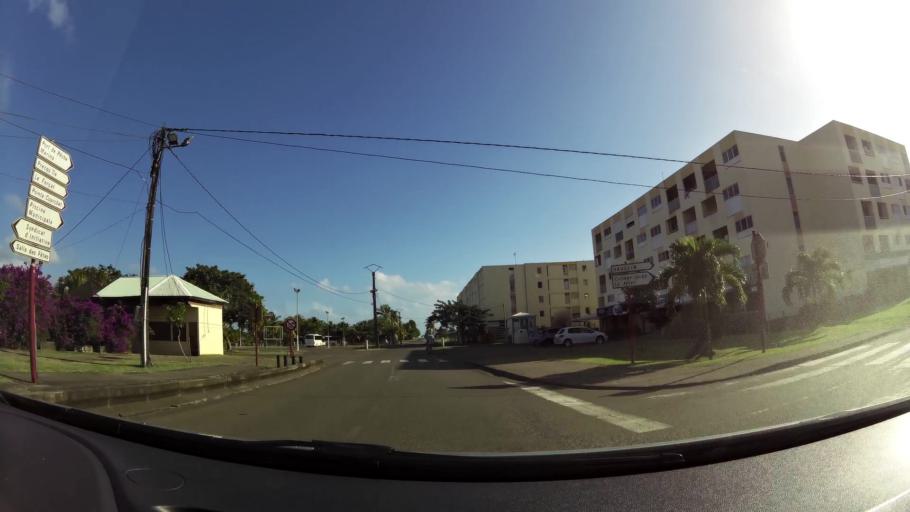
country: MQ
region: Martinique
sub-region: Martinique
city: Le Francois
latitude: 14.6175
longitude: -60.9000
